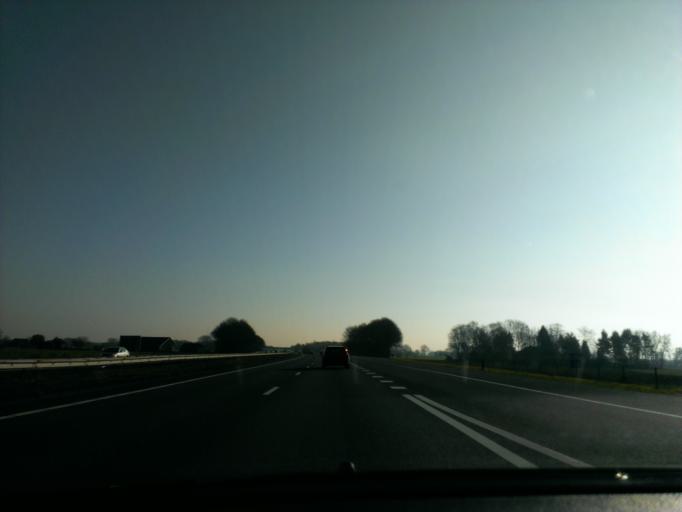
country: NL
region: Gelderland
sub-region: Gemeente Lochem
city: Laren
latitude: 52.2460
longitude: 6.3772
